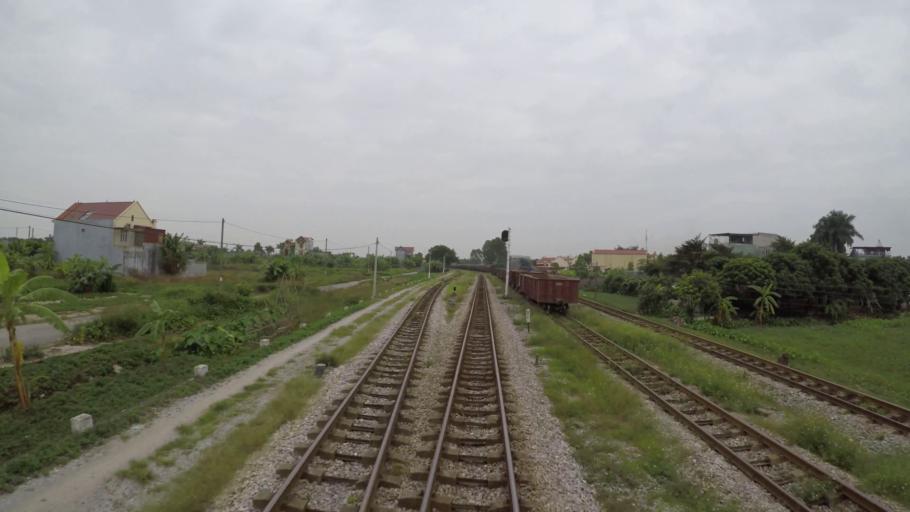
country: VN
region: Hai Phong
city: An Duong
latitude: 20.9073
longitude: 106.5735
